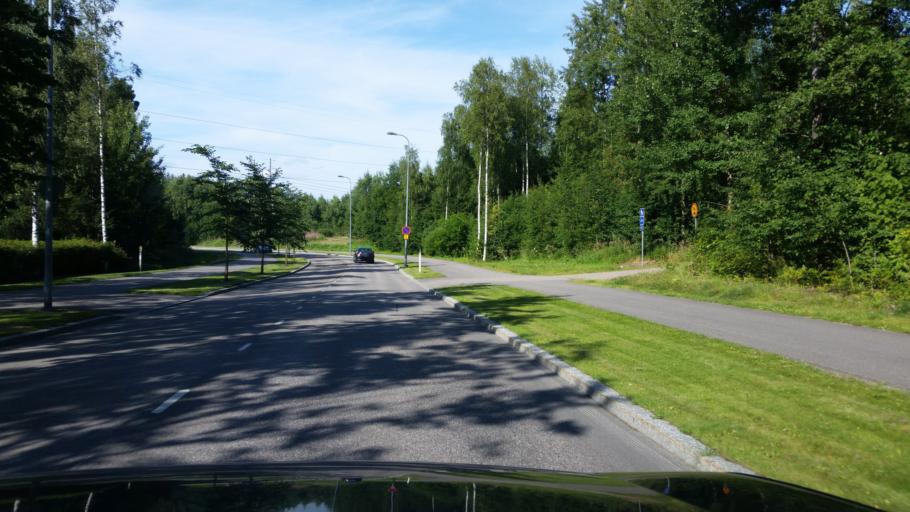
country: FI
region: Uusimaa
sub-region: Helsinki
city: Vantaa
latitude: 60.3312
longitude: 25.0270
